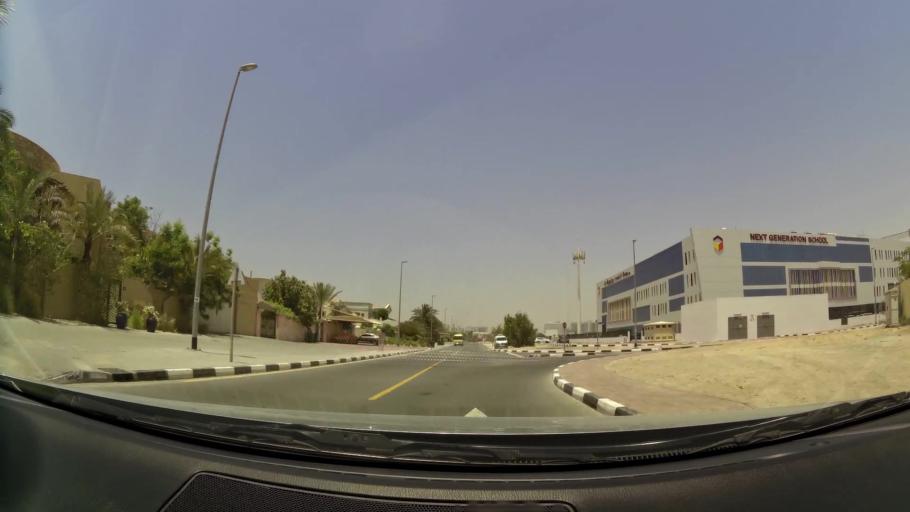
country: AE
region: Dubai
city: Dubai
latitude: 25.0990
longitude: 55.1880
